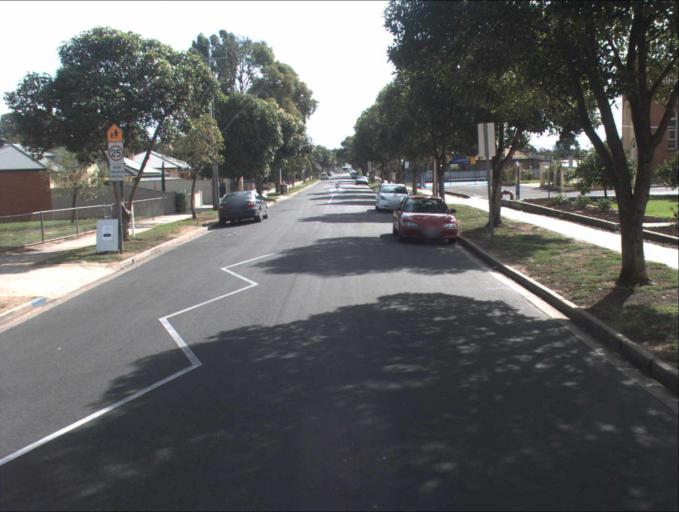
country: AU
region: South Australia
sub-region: Port Adelaide Enfield
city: Blair Athol
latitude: -34.8619
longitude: 138.5884
